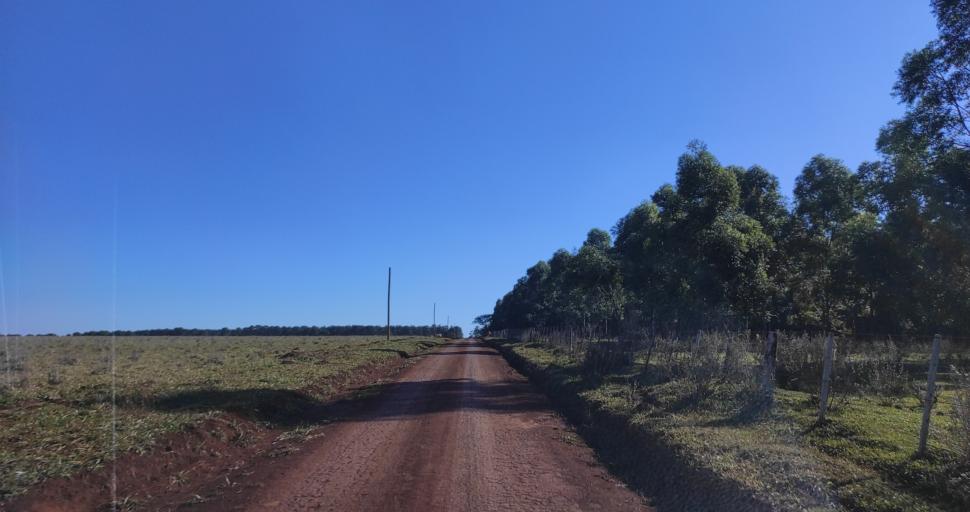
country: PY
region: Itapua
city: San Juan del Parana
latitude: -27.4235
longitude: -56.0869
